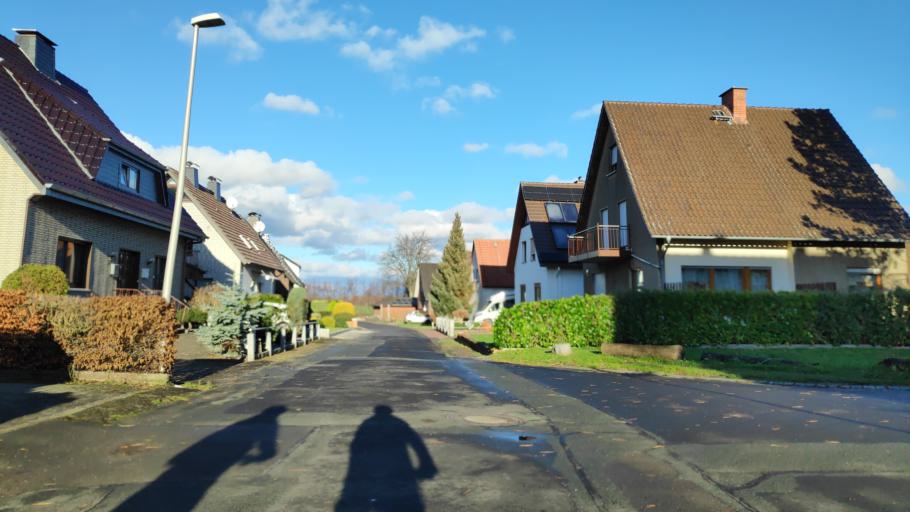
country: DE
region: North Rhine-Westphalia
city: Bad Oeynhausen
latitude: 52.2720
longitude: 8.8241
